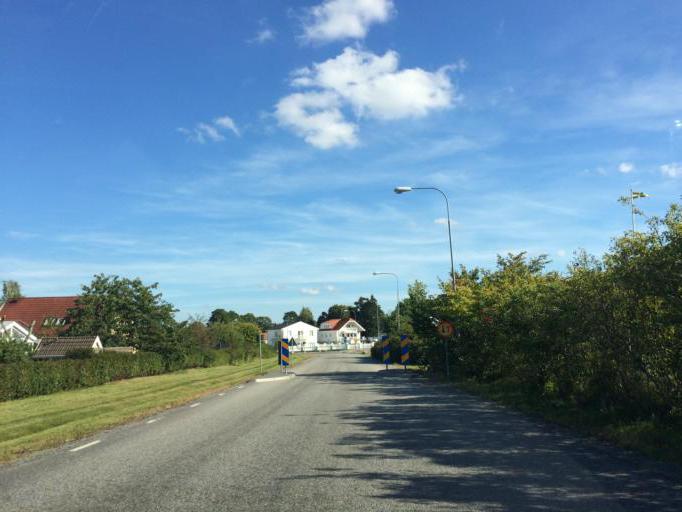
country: SE
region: Stockholm
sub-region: Upplands Vasby Kommun
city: Upplands Vaesby
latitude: 59.4928
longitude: 17.9455
